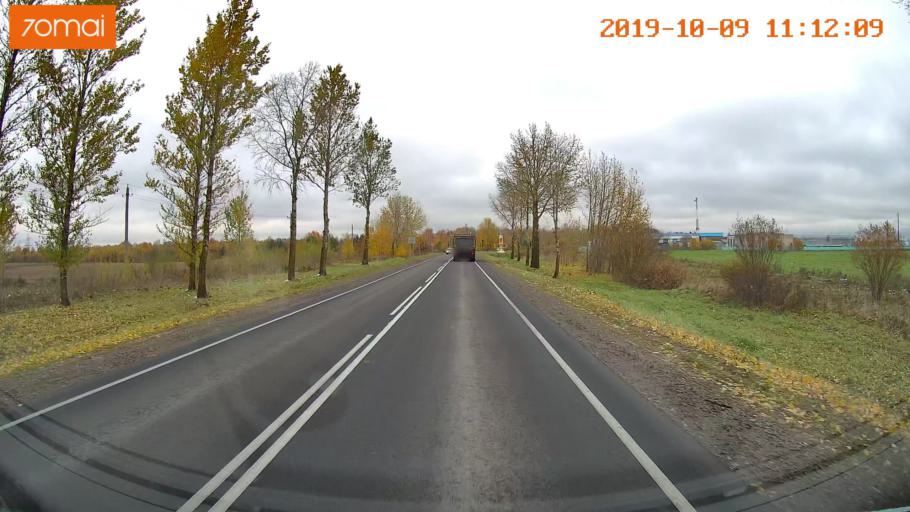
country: RU
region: Vologda
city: Vologda
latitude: 59.1748
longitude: 39.8270
